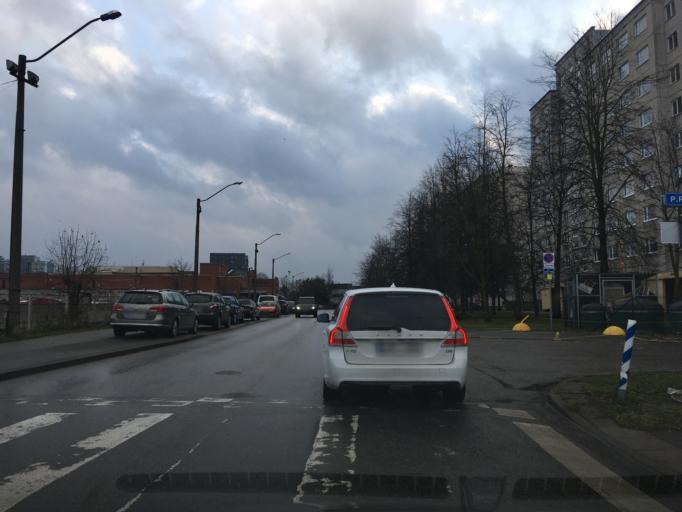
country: EE
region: Harju
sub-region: Tallinna linn
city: Kose
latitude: 59.4395
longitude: 24.8366
